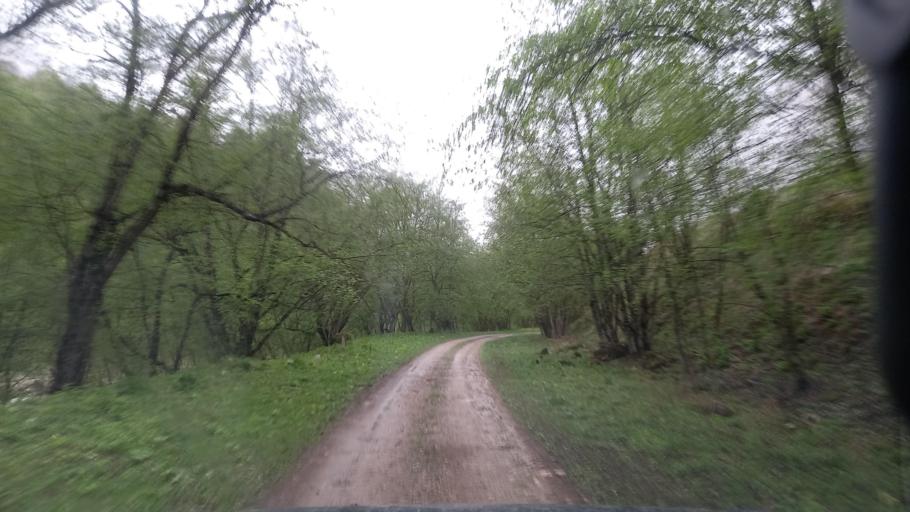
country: RU
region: Kabardino-Balkariya
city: Bylym
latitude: 43.5949
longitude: 42.9634
